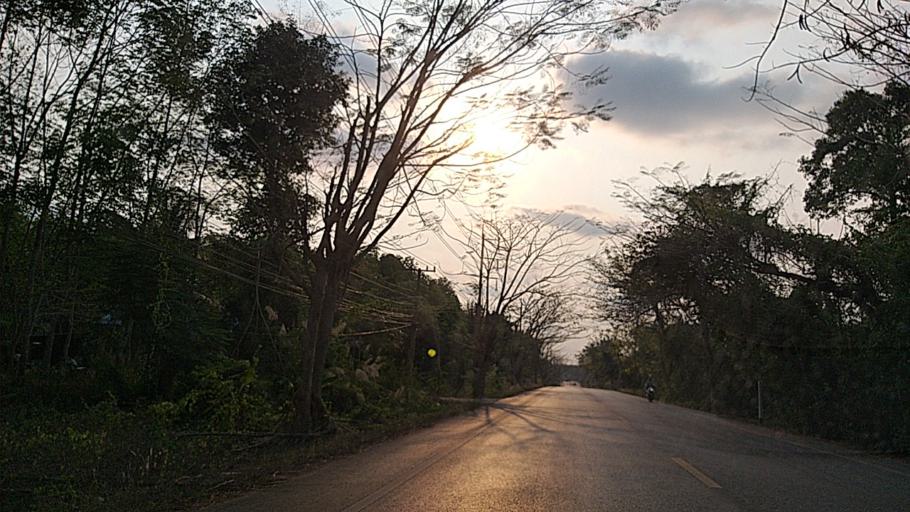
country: TH
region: Trat
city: Khao Saming
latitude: 12.2898
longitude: 102.3268
